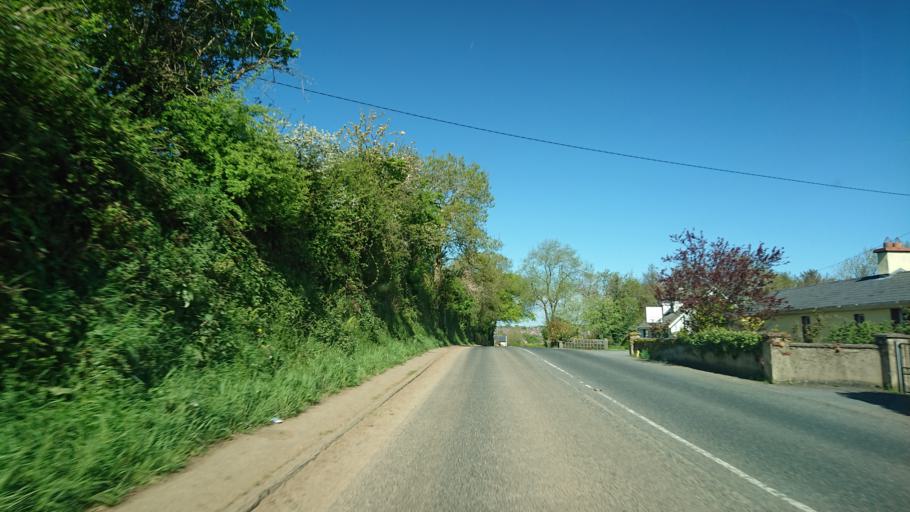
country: IE
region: Munster
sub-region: Waterford
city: Waterford
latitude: 52.2341
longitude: -7.0529
